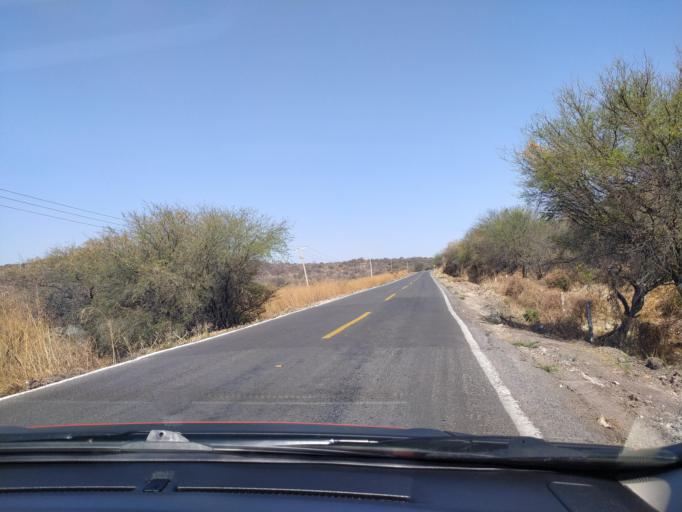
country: MX
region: Guanajuato
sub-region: San Francisco del Rincon
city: San Ignacio de Hidalgo
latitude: 20.7975
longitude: -101.8365
